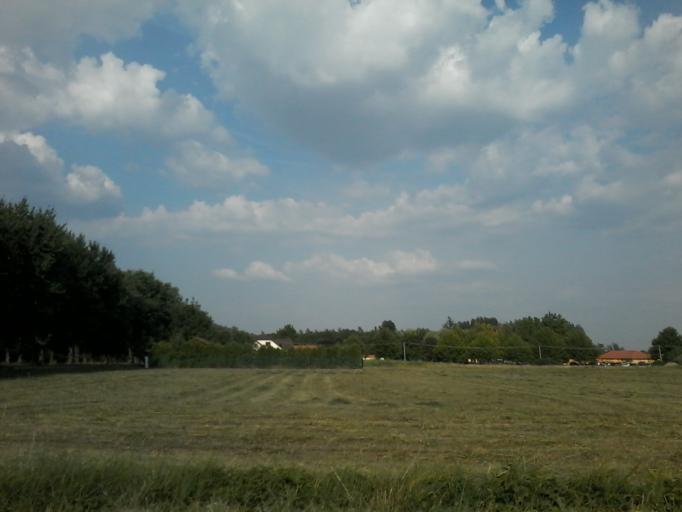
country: HU
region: Vas
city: Celldomolk
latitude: 47.2181
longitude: 17.0898
